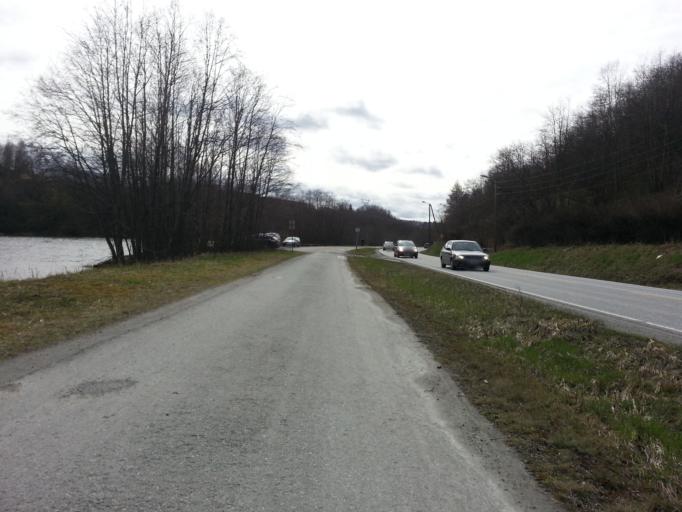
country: NO
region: Sor-Trondelag
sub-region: Trondheim
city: Trondheim
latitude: 63.4007
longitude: 10.3885
